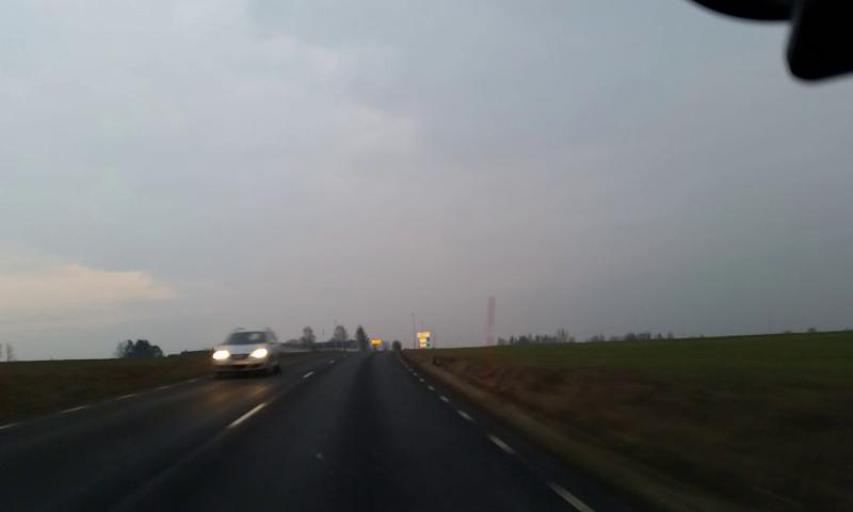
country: SE
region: Skane
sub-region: Angelholms Kommun
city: AEngelholm
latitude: 56.2630
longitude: 12.8877
